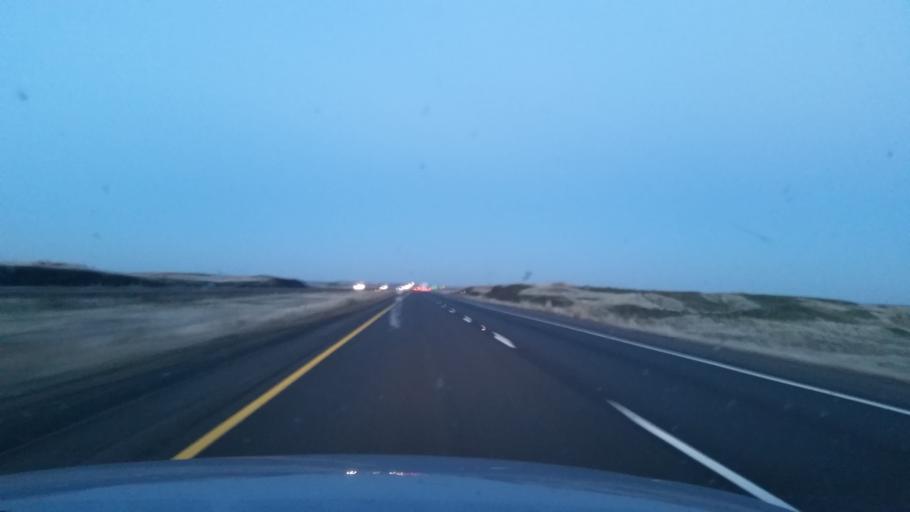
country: US
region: Washington
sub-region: Adams County
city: Ritzville
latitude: 47.1443
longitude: -118.3258
